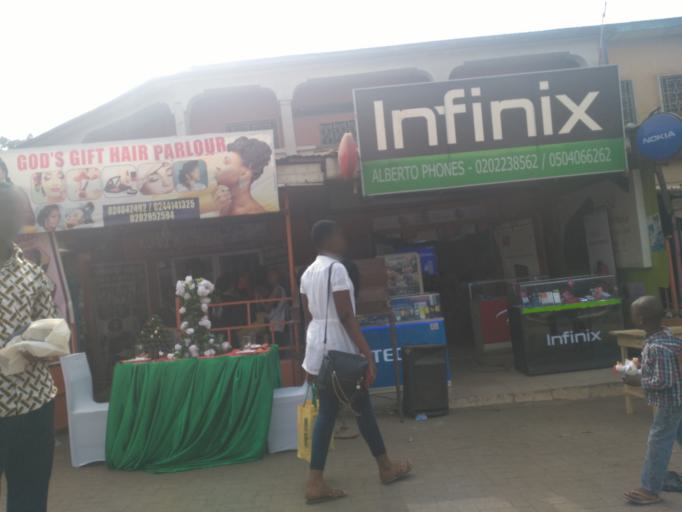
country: GH
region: Ashanti
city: Kumasi
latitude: 6.7087
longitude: -1.6374
